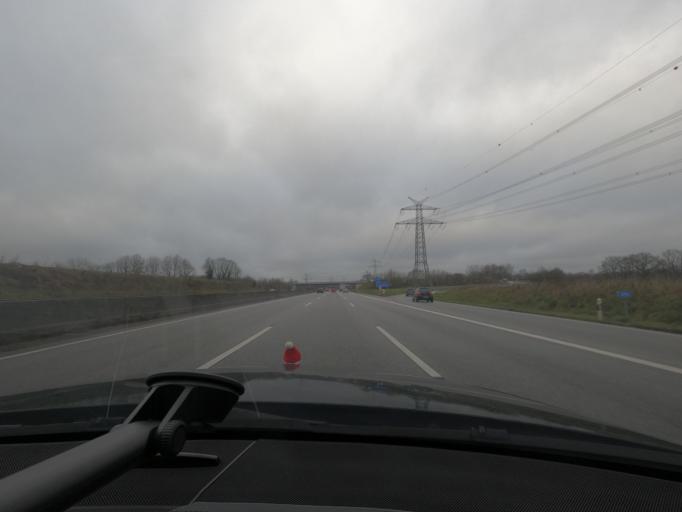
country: DE
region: Schleswig-Holstein
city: Alveslohe
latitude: 53.8016
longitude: 9.9302
